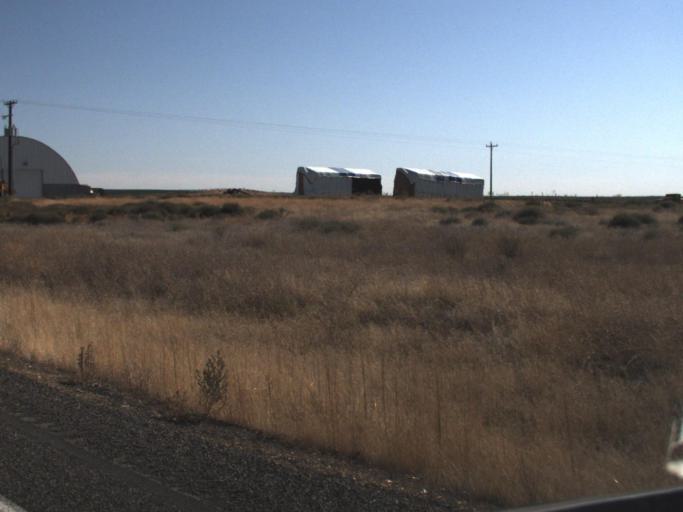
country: US
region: Washington
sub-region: Walla Walla County
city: Burbank
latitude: 46.2153
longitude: -118.9309
